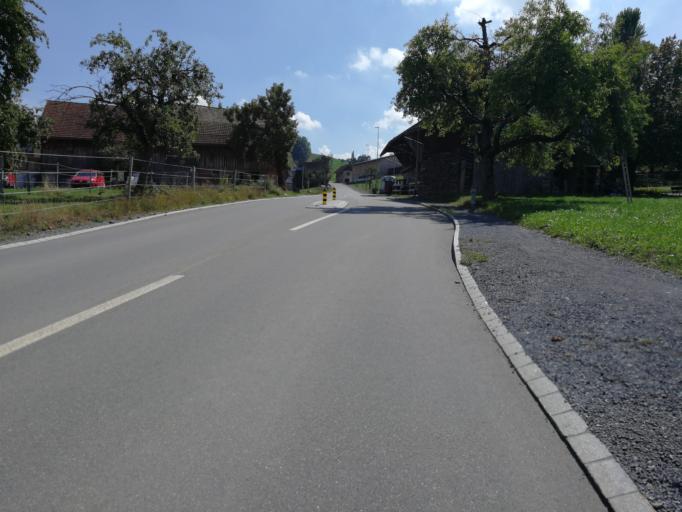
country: CH
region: Zurich
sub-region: Bezirk Horgen
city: Au / Unter-Dorf
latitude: 47.2426
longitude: 8.6242
